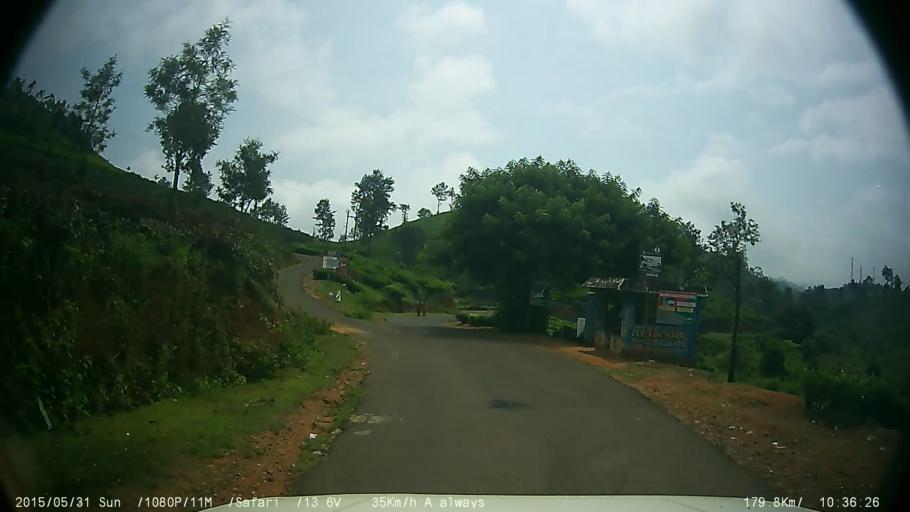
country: IN
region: Kerala
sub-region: Wayanad
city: Kalpetta
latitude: 11.5045
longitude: 76.1479
